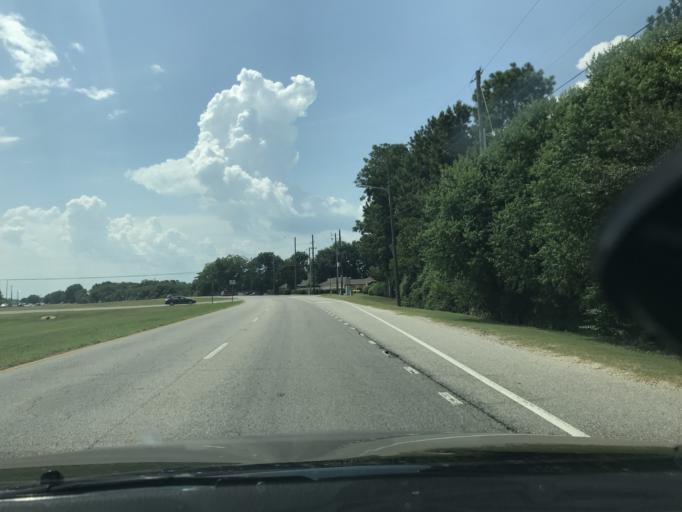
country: US
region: Alabama
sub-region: Montgomery County
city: Pike Road
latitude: 32.3814
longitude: -86.1604
